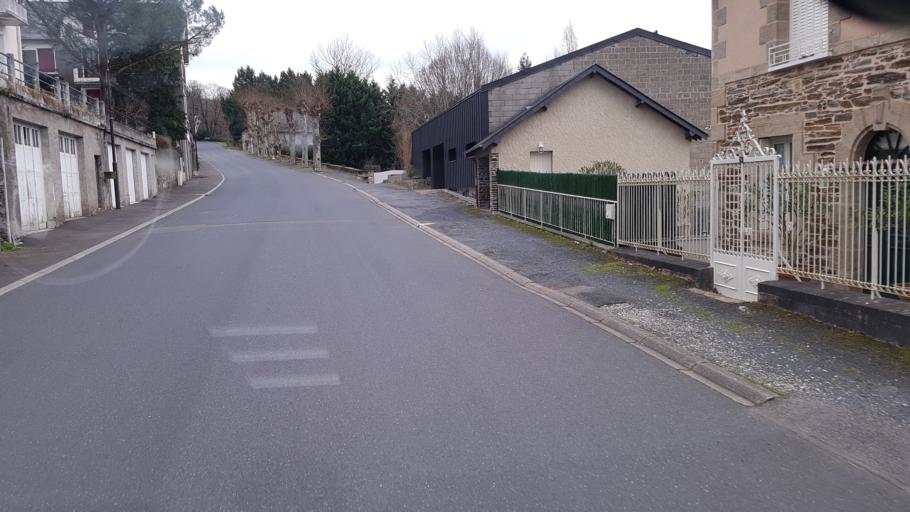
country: FR
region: Limousin
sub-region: Departement de la Correze
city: Donzenac
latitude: 45.2293
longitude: 1.5249
